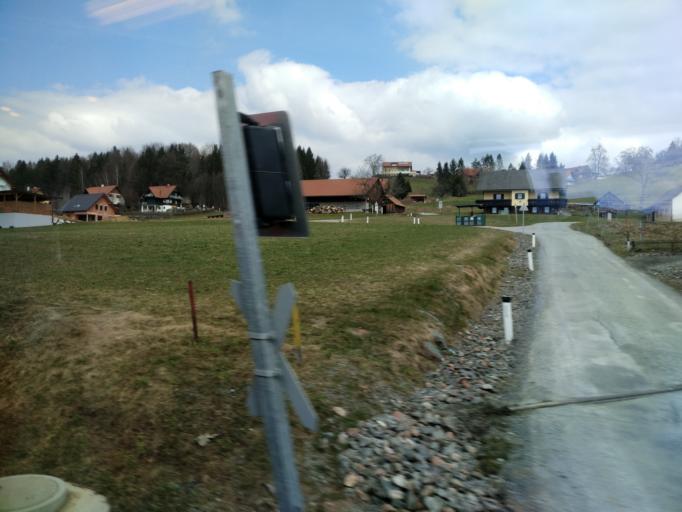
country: AT
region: Styria
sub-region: Politischer Bezirk Deutschlandsberg
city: Hollenegg
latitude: 46.7961
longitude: 15.2334
